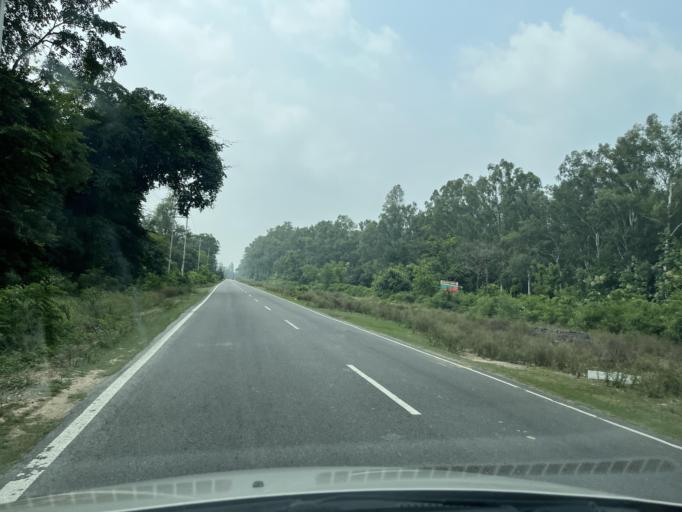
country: IN
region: Uttarakhand
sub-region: Haridwar
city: Sultanpur
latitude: 29.7571
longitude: 78.2673
